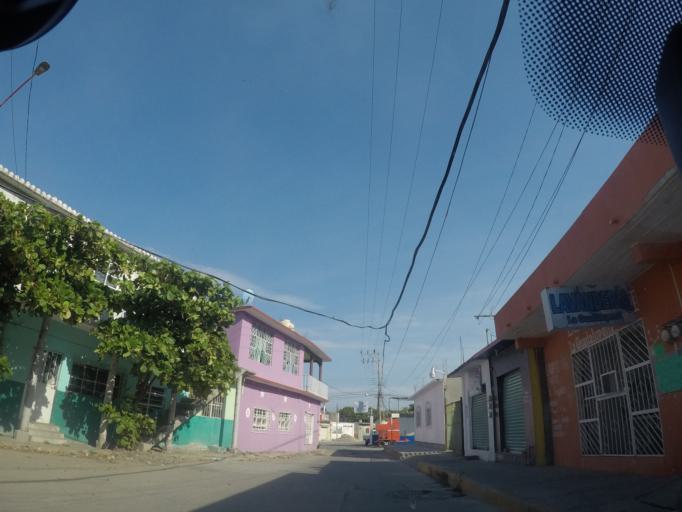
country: MX
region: Oaxaca
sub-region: Salina Cruz
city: Salina Cruz
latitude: 16.1768
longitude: -95.1977
